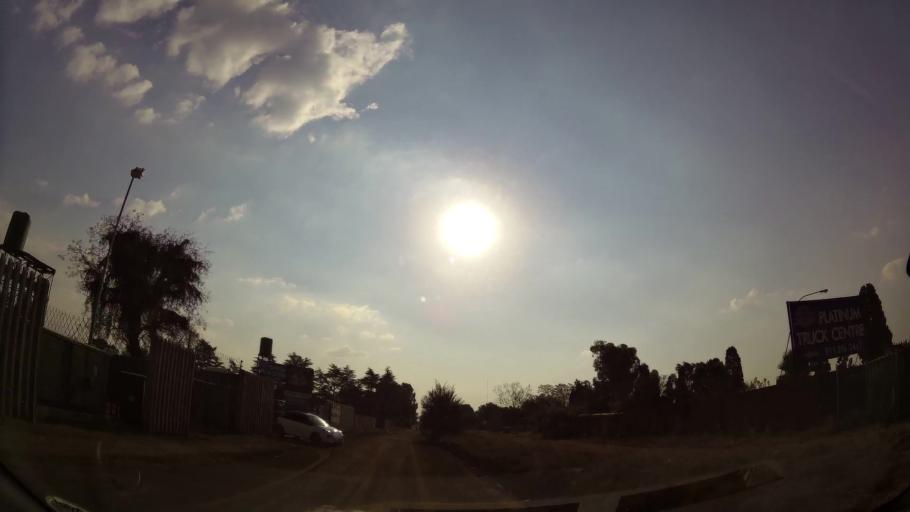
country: ZA
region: Gauteng
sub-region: Ekurhuleni Metropolitan Municipality
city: Benoni
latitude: -26.0953
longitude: 28.2969
